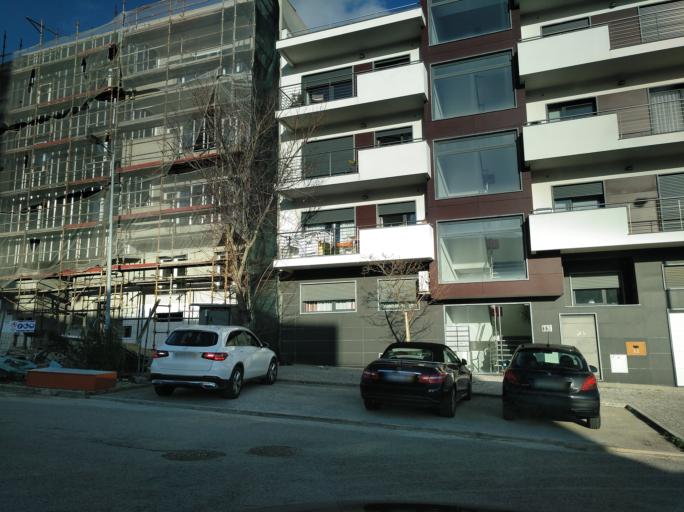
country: PT
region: Setubal
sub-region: Almada
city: Sobreda
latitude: 38.6433
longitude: -9.1858
